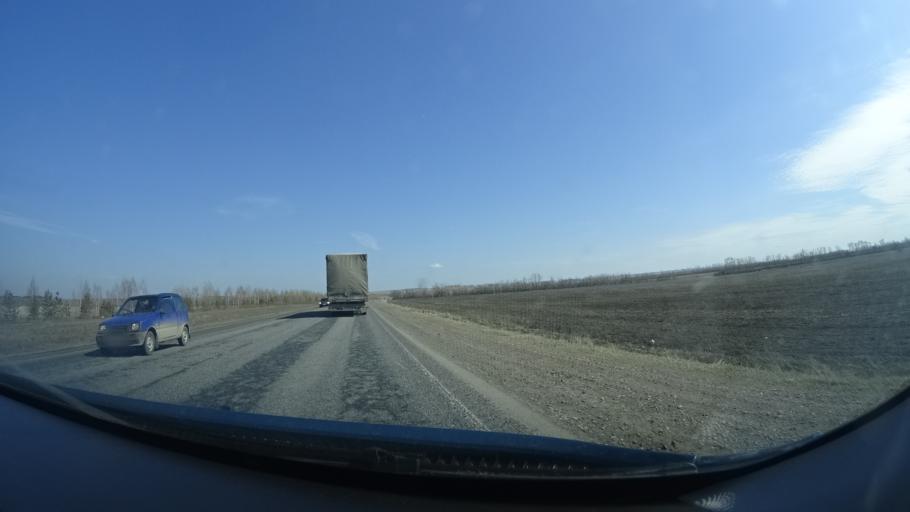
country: RU
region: Bashkortostan
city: Subkhankulovo
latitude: 54.4847
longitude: 53.8737
